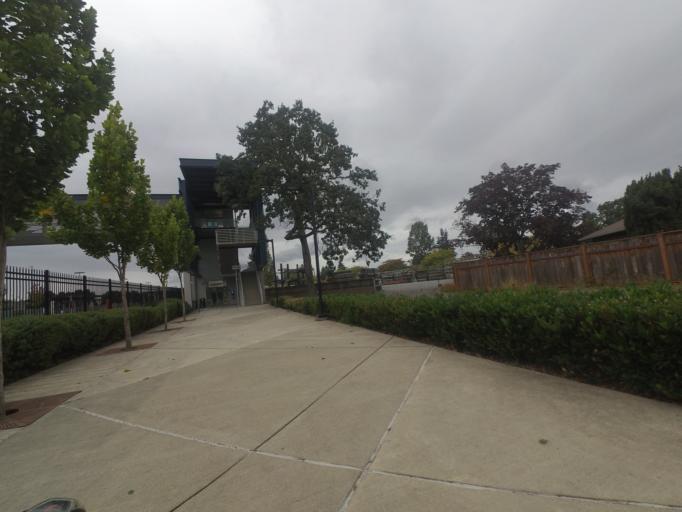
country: US
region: Washington
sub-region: Pierce County
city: McChord Air Force Base
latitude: 47.1540
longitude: -122.4982
